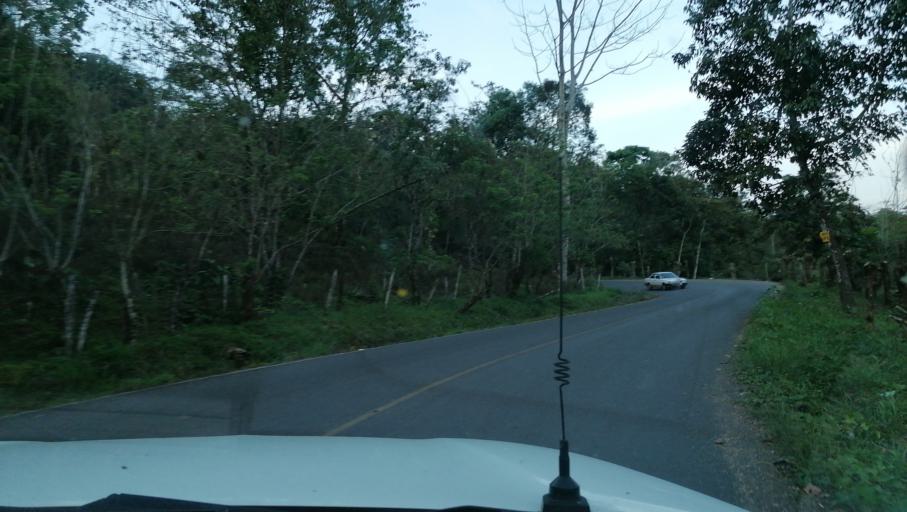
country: MX
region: Chiapas
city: Ostuacan
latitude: 17.4250
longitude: -93.3402
